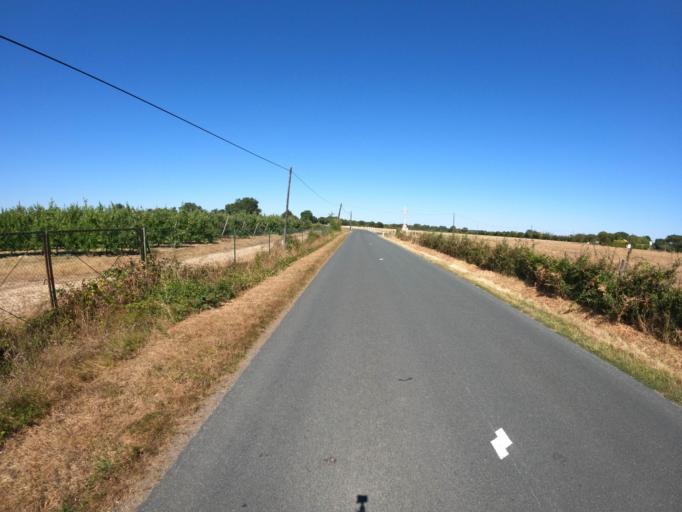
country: FR
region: Pays de la Loire
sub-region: Departement de la Vendee
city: La Boissiere-de-Montaigu
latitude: 46.9523
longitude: -1.1762
